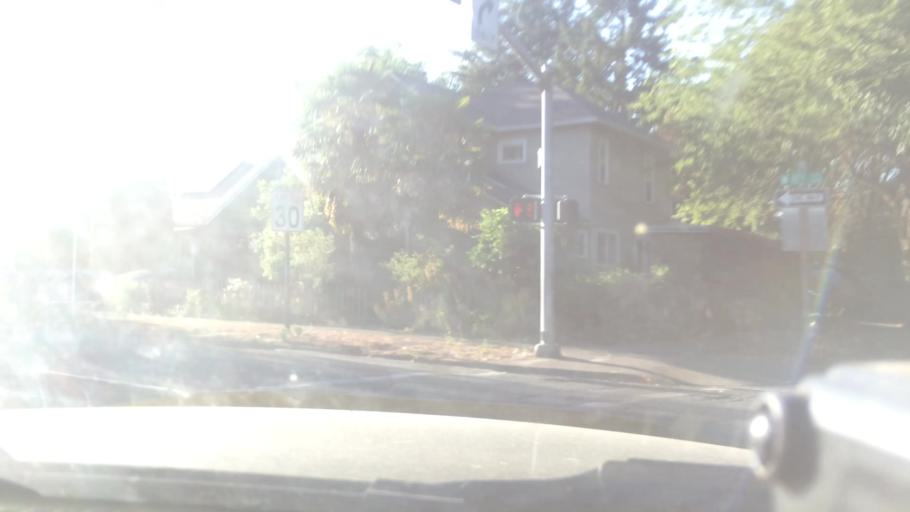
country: US
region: Oregon
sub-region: Lane County
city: Eugene
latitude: 44.0477
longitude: -123.1126
